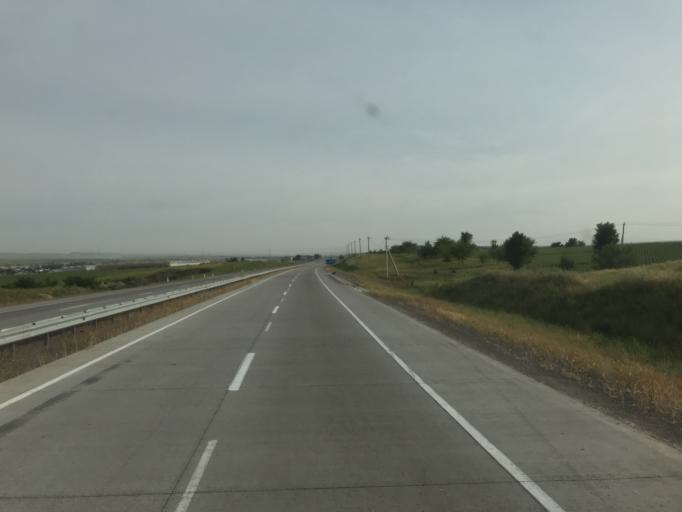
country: KZ
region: Ongtustik Qazaqstan
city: Qazyqurt
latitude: 41.6791
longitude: 69.3936
